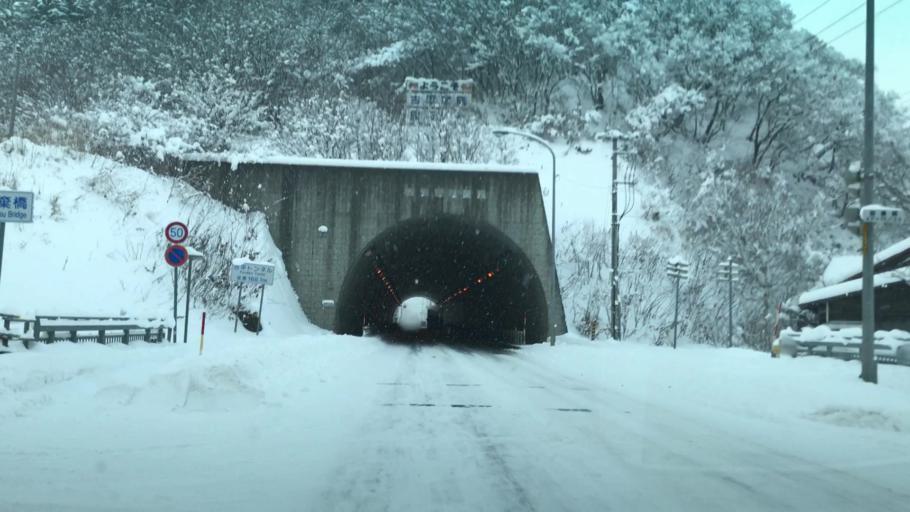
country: JP
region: Hokkaido
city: Yoichi
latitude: 43.2604
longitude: 140.6540
